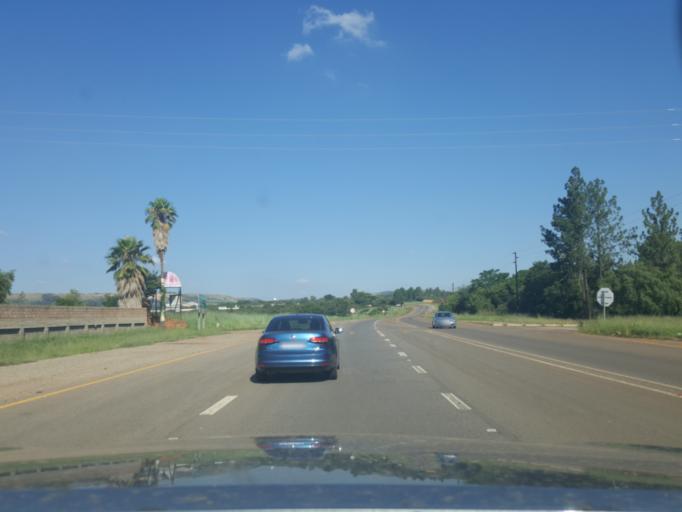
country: ZA
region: Gauteng
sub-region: City of Tshwane Metropolitan Municipality
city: Cullinan
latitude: -25.7616
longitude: 28.4190
